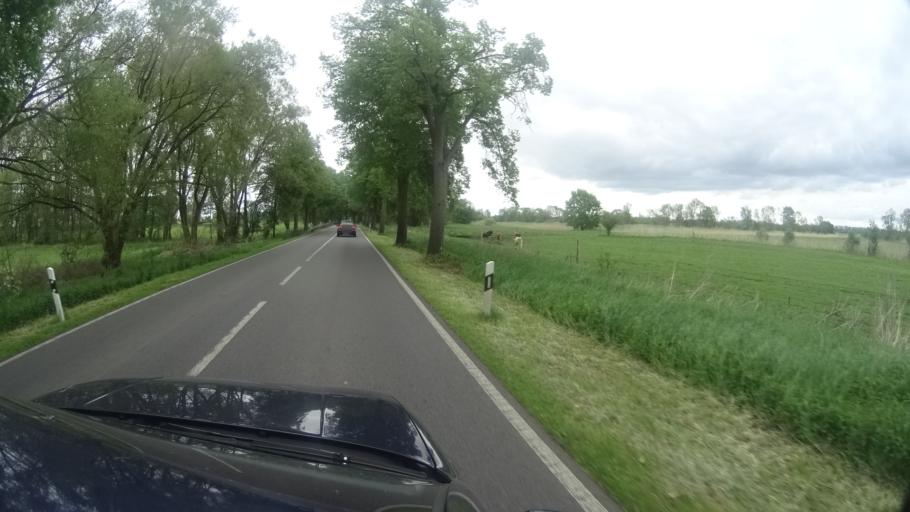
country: DE
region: Brandenburg
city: Fehrbellin
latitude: 52.8308
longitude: 12.7764
